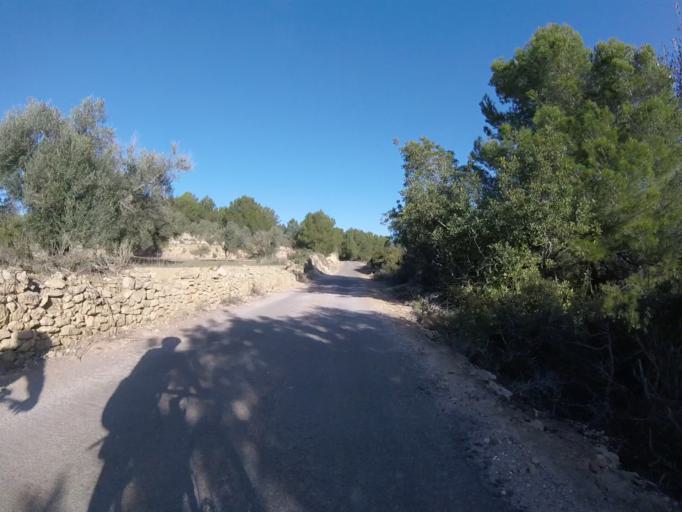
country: ES
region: Valencia
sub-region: Provincia de Castello
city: Alcala de Xivert
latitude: 40.2718
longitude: 0.2064
